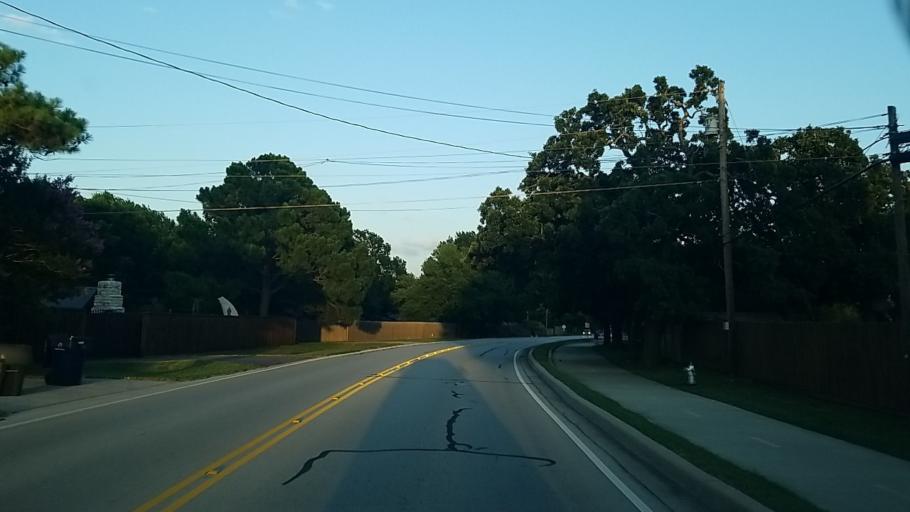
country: US
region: Texas
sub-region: Denton County
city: Highland Village
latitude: 33.0919
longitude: -97.0369
